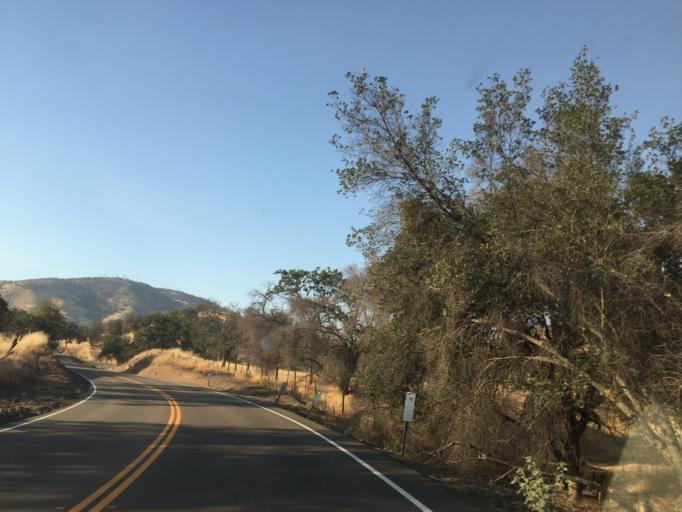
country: US
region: California
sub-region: Fresno County
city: Squaw Valley
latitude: 36.7136
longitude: -119.2861
